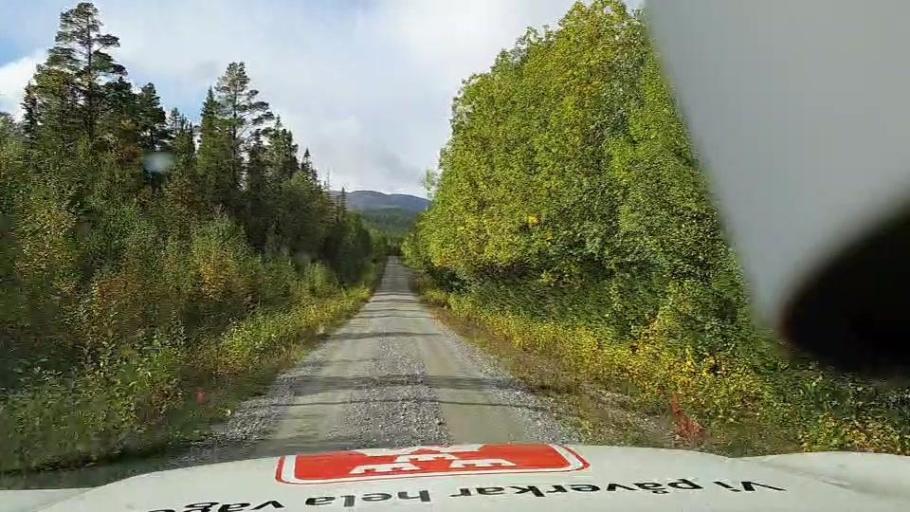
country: SE
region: Jaemtland
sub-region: Are Kommun
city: Jarpen
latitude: 63.1779
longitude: 13.4723
